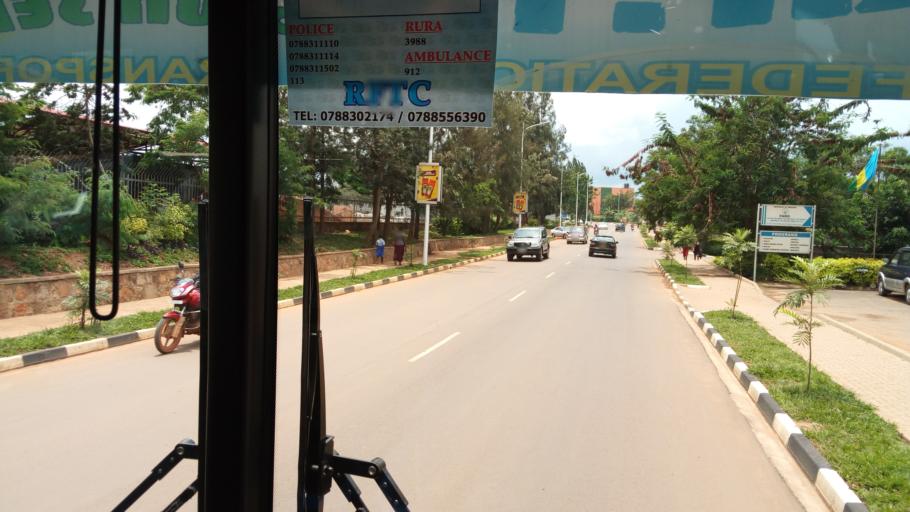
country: RW
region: Kigali
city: Kigali
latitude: -1.9565
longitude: 30.1158
